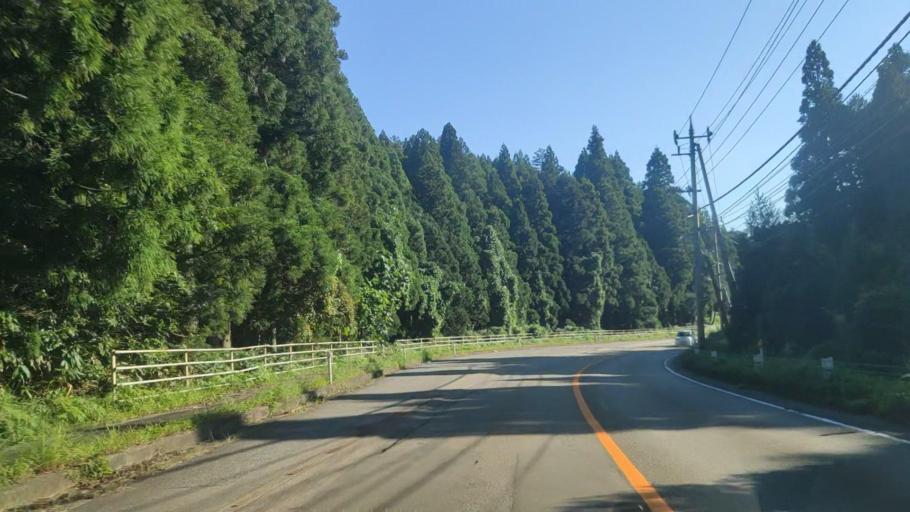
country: JP
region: Ishikawa
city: Nanao
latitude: 37.1215
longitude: 136.8624
